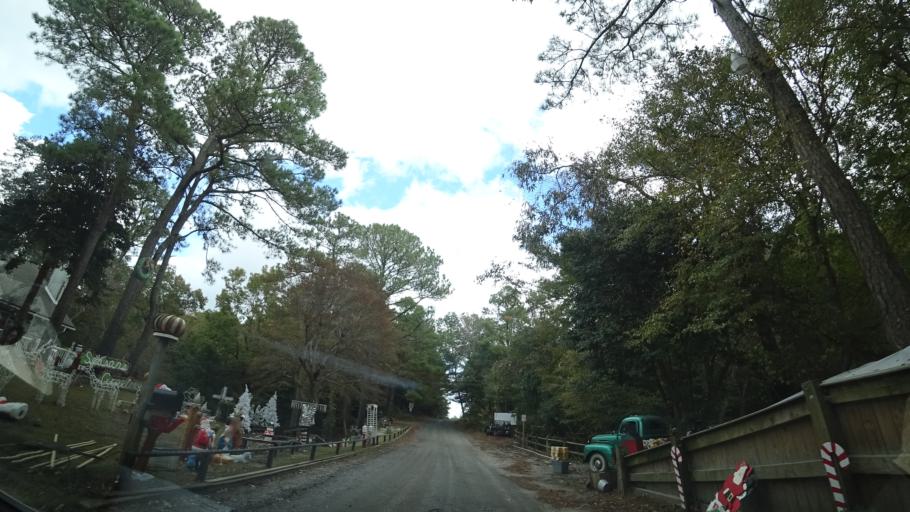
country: US
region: North Carolina
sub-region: Dare County
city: Kill Devil Hills
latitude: 35.9901
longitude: -75.6618
